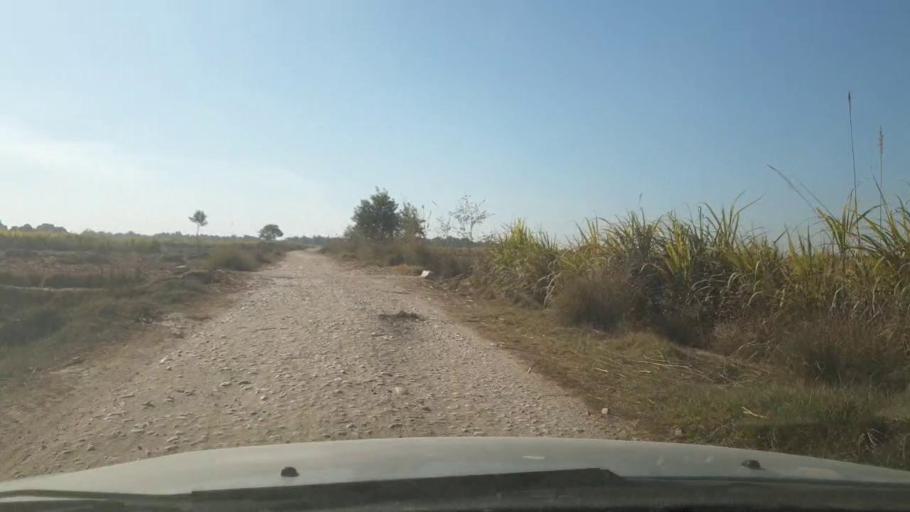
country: PK
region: Sindh
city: Ghotki
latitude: 27.9783
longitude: 69.1957
